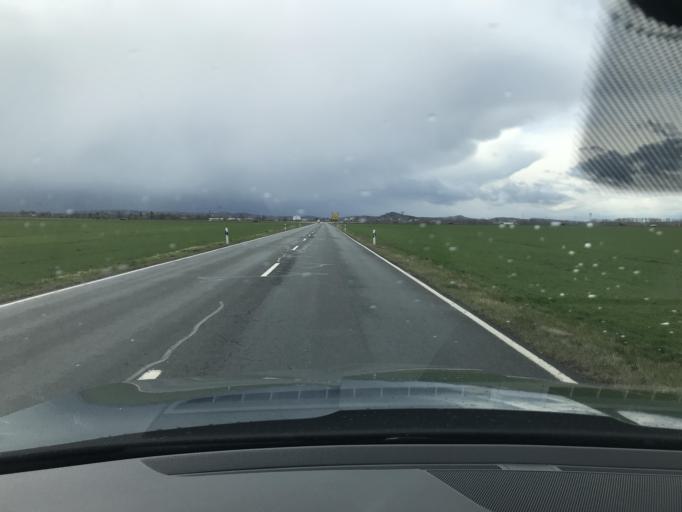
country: DE
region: Saxony-Anhalt
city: Quedlinburg
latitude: 51.7899
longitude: 11.1899
